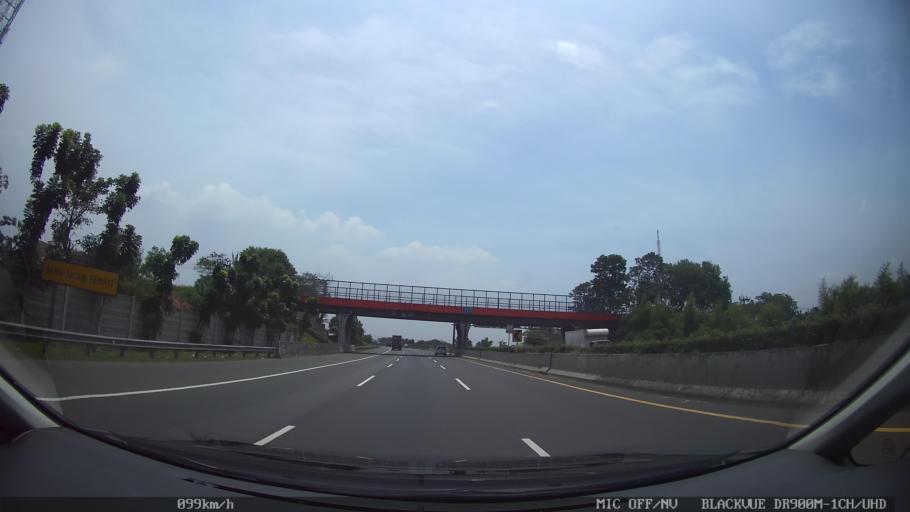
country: ID
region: West Java
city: Kresek
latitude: -6.1778
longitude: 106.3867
